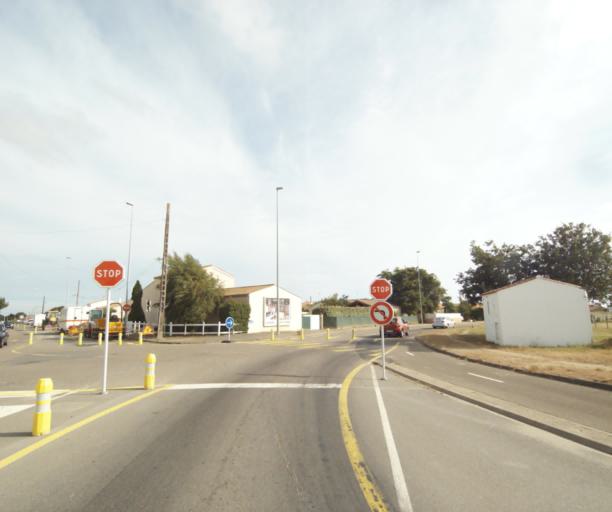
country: FR
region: Pays de la Loire
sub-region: Departement de la Vendee
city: Chateau-d'Olonne
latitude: 46.4864
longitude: -1.7316
